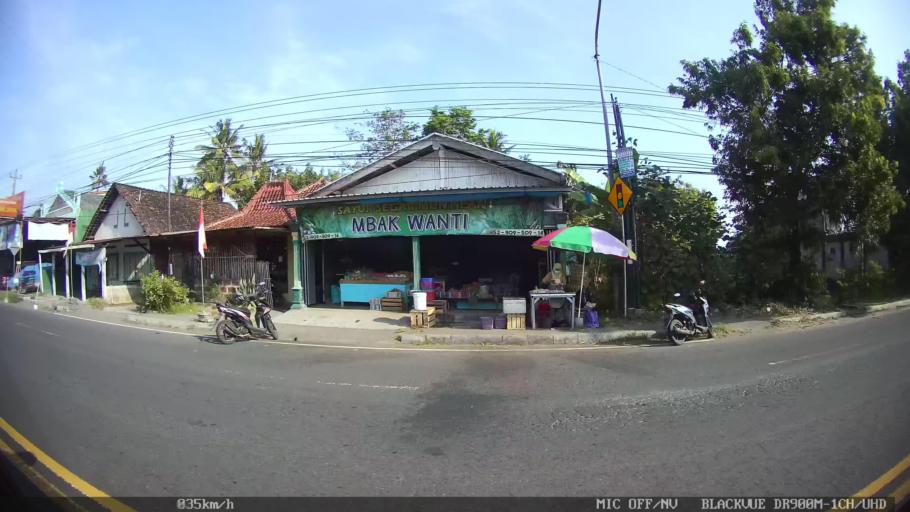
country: ID
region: Daerah Istimewa Yogyakarta
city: Bantul
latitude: -7.9059
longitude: 110.3157
